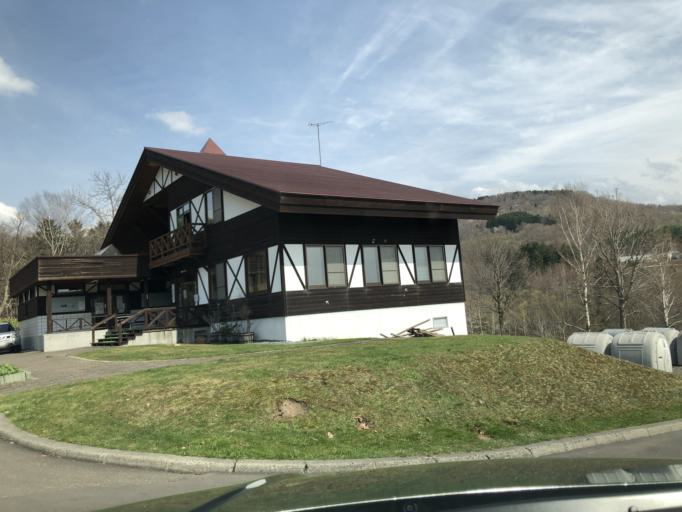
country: JP
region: Hokkaido
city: Akabira
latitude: 43.5945
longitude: 142.0469
